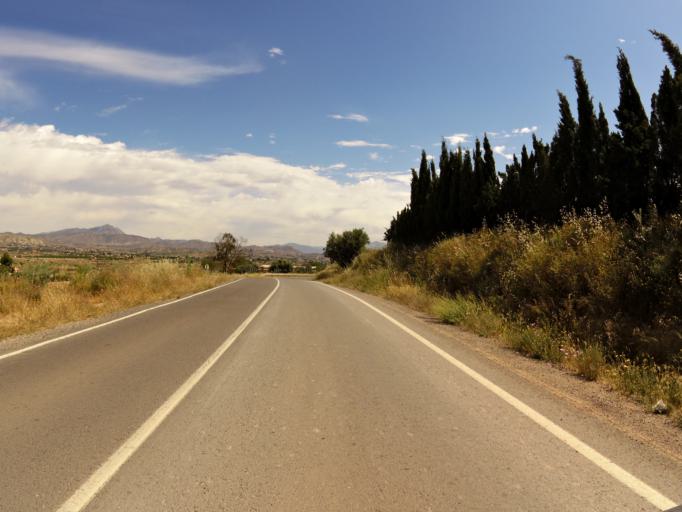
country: ES
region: Valencia
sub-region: Provincia de Alicante
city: Agost
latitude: 38.3938
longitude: -0.5971
